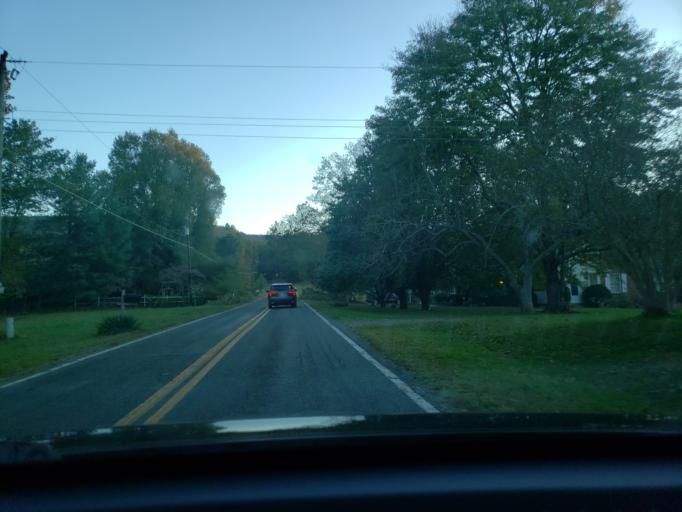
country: US
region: North Carolina
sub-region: Stokes County
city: Danbury
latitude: 36.4184
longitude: -80.2447
